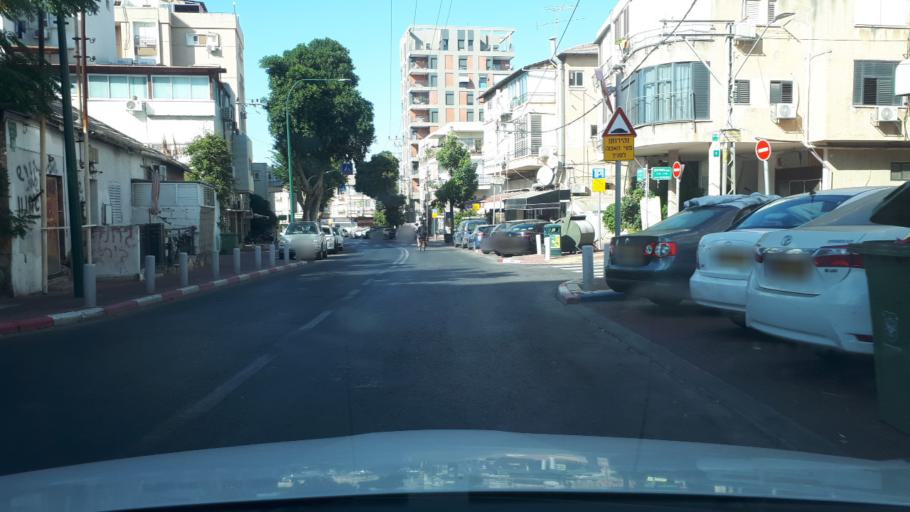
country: IL
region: Tel Aviv
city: Giv`atayim
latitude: 32.0723
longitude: 34.8231
